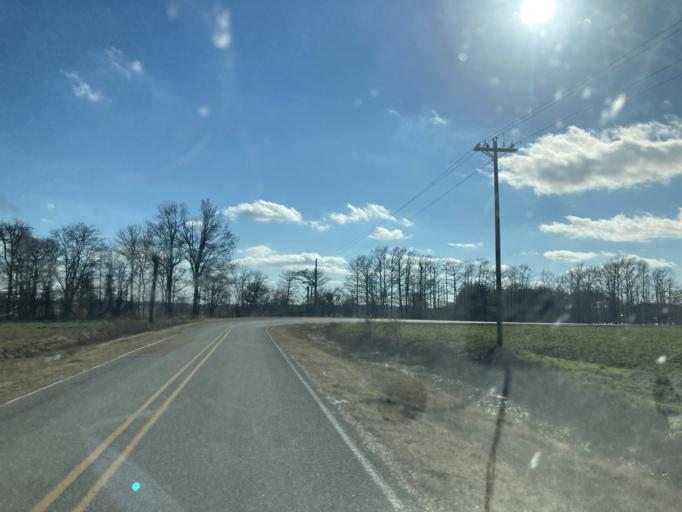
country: US
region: Mississippi
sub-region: Yazoo County
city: Yazoo City
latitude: 32.9601
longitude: -90.4943
